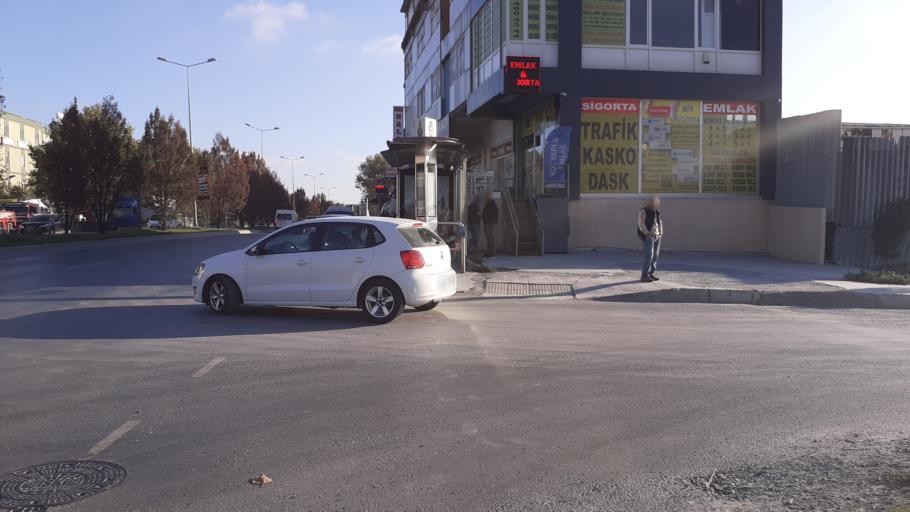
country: TR
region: Istanbul
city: Basaksehir
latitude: 41.0804
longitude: 28.7856
